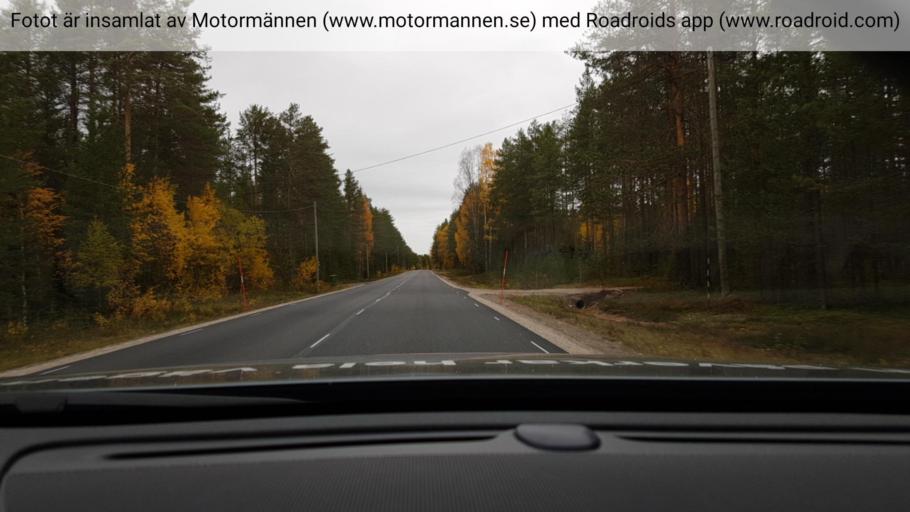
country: SE
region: Norrbotten
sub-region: Overkalix Kommun
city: OEverkalix
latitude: 66.4260
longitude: 22.7967
